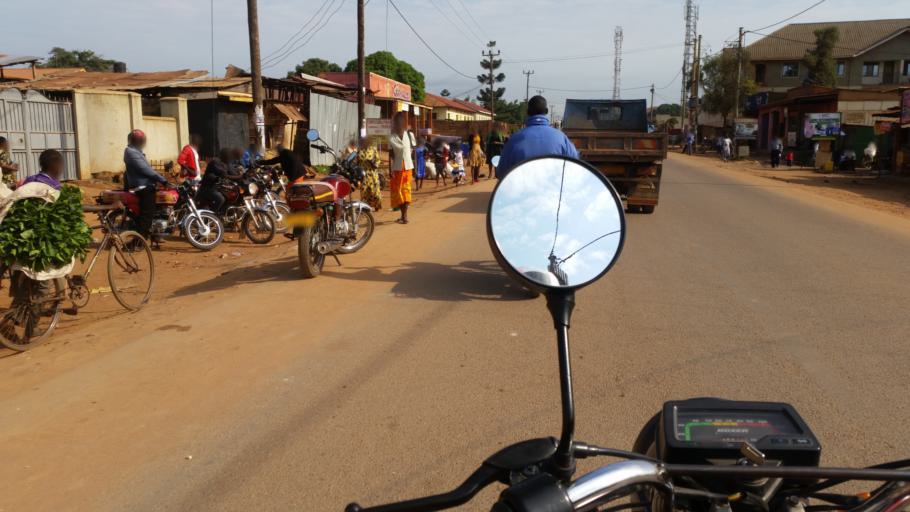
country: UG
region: Central Region
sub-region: Mukono District
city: Mukono
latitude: 0.3708
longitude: 32.7127
